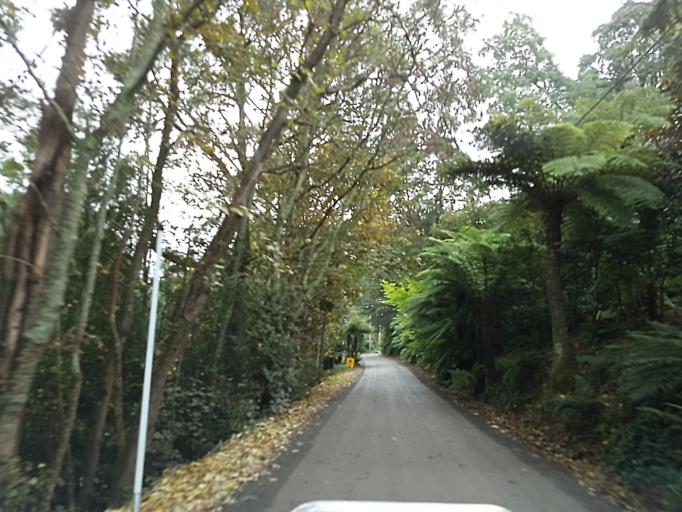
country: AU
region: Victoria
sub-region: Yarra Ranges
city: Monbulk
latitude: -37.8805
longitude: 145.3873
